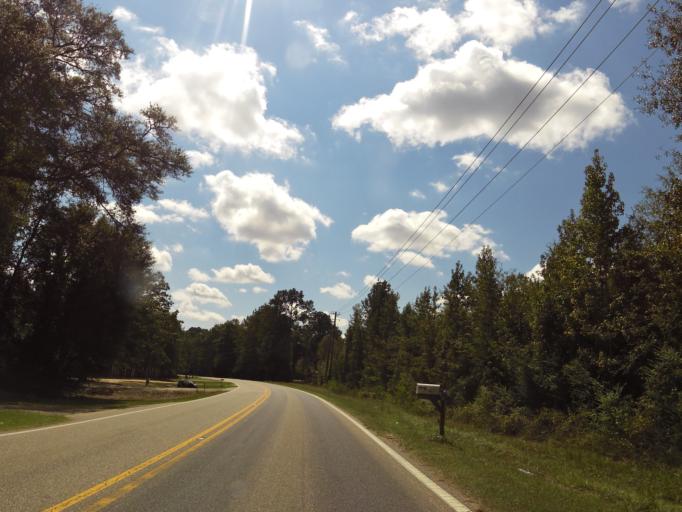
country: US
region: Alabama
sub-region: Dallas County
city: Selma
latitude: 32.3980
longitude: -87.0889
